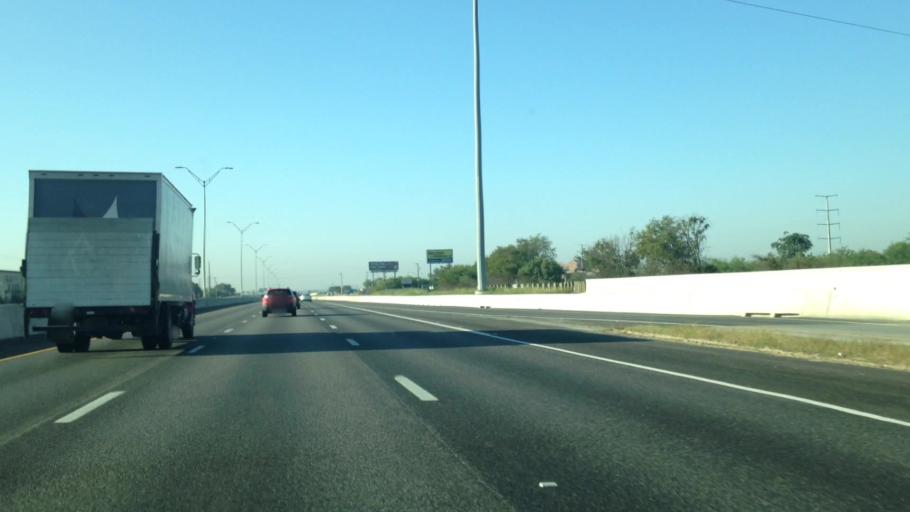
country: US
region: Texas
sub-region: Bexar County
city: Kirby
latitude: 29.4705
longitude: -98.4062
